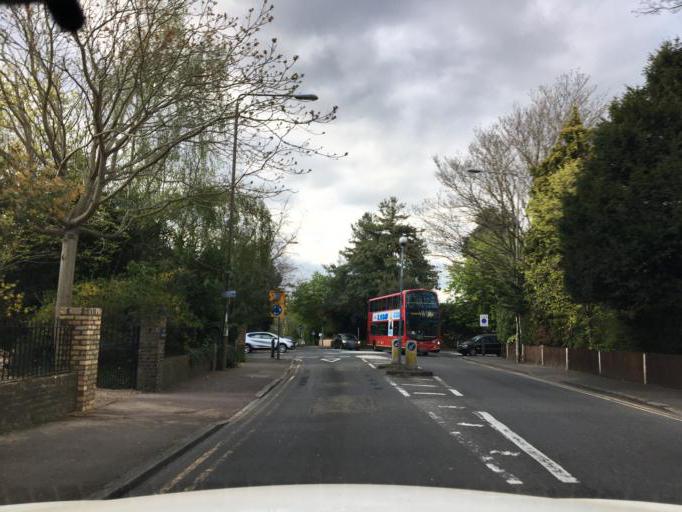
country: GB
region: England
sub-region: Greater London
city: Chislehurst
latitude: 51.4477
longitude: 0.0525
